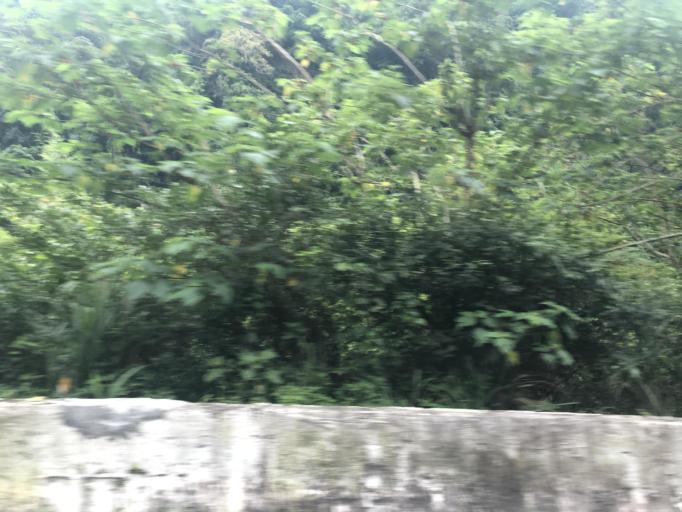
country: TW
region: Taiwan
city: Daxi
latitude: 24.8606
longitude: 121.4339
